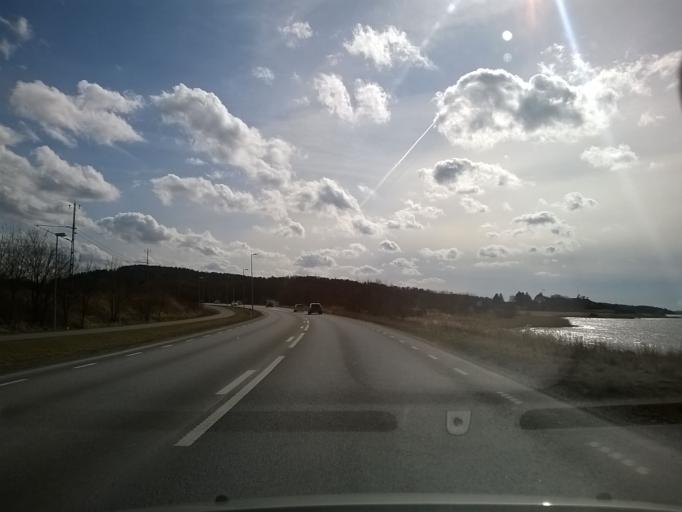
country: SE
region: Vaestra Goetaland
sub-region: Stenungsunds Kommun
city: Stora Hoga
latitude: 58.0384
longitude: 11.8213
